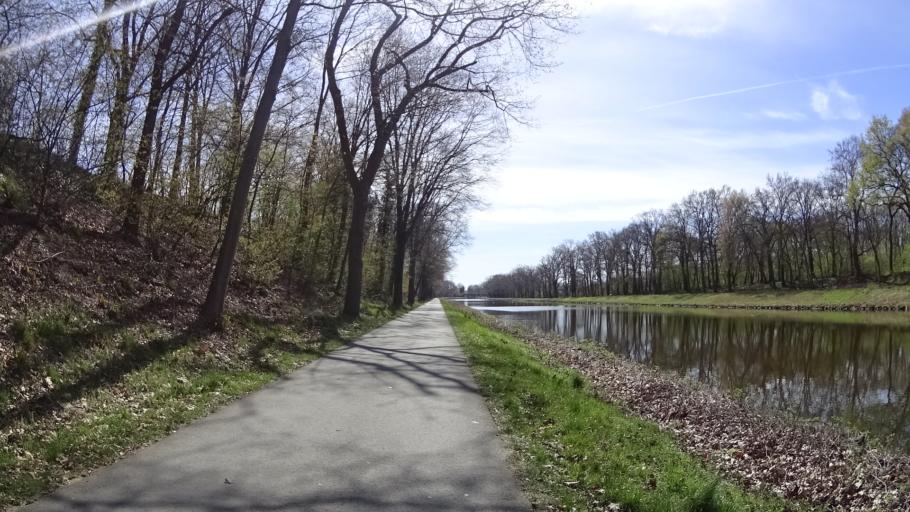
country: DE
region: Lower Saxony
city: Lingen
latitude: 52.5331
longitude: 7.3024
